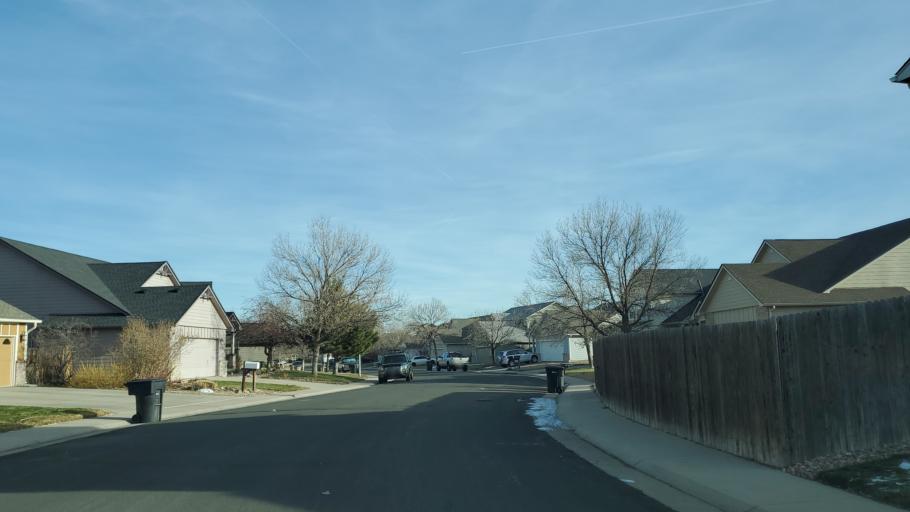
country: US
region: Colorado
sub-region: Adams County
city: Northglenn
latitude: 39.9079
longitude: -104.9581
